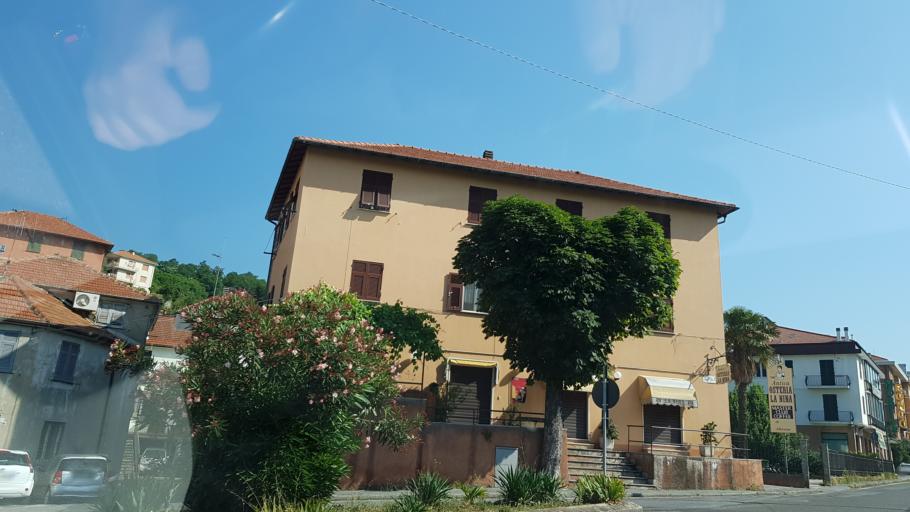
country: IT
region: Liguria
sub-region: Provincia di Genova
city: Pedemonte
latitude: 44.4986
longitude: 8.9229
